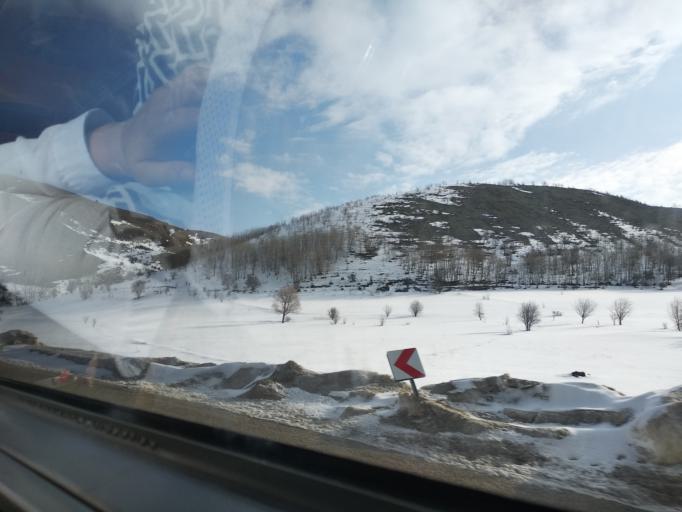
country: TR
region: Erzincan
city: Catalarmut
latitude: 39.9111
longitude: 39.4093
